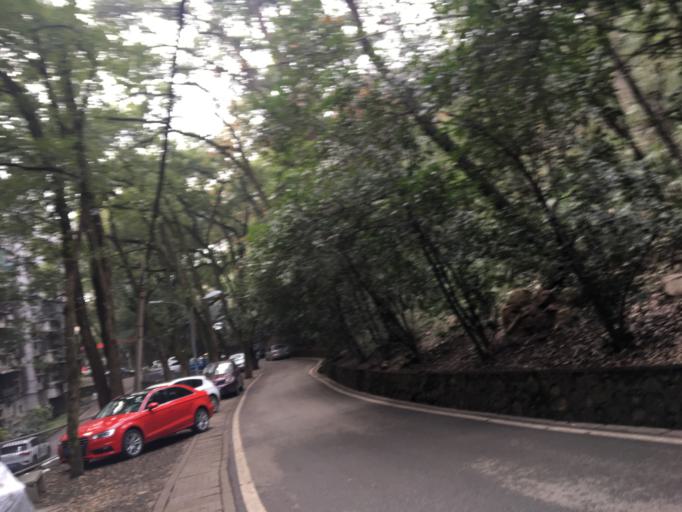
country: CN
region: Hubei
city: Guanshan
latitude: 30.5357
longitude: 114.3674
